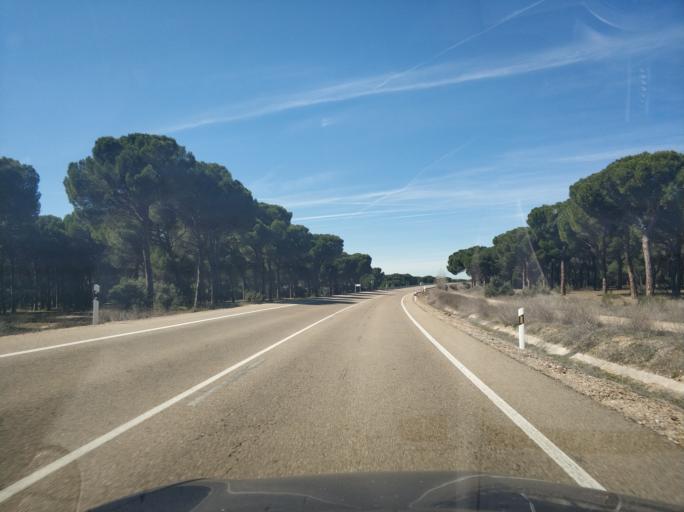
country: ES
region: Castille and Leon
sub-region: Provincia de Valladolid
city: Viana de Cega
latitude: 41.5325
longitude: -4.7503
